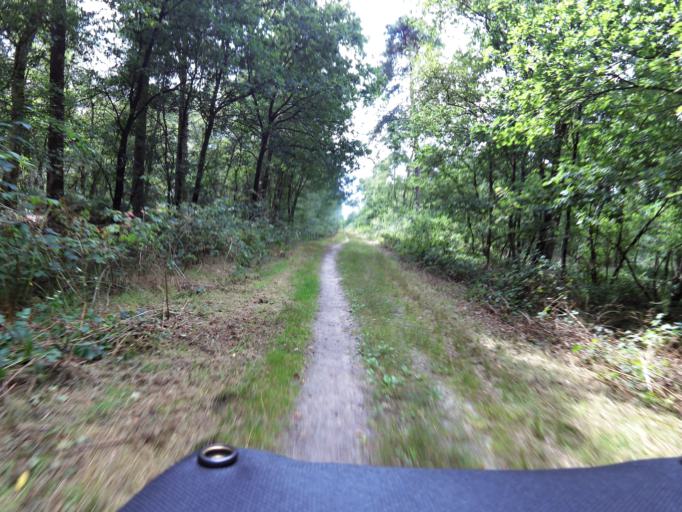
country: BE
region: Flanders
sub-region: Provincie Antwerpen
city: Baarle-Hertog
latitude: 51.4146
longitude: 4.8391
